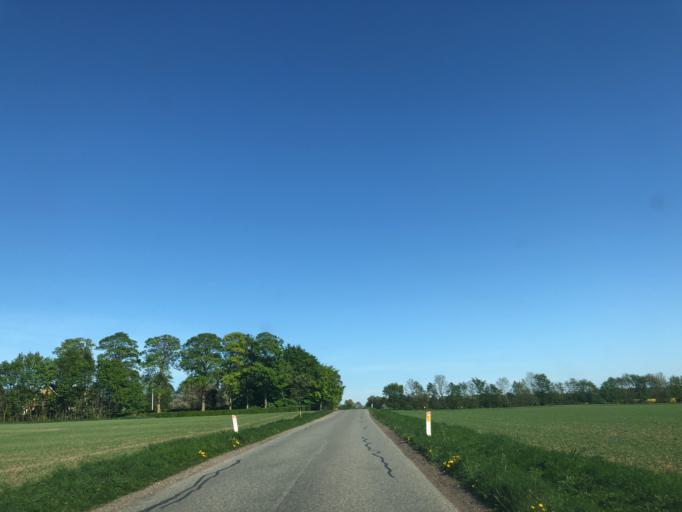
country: DK
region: Zealand
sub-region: Ringsted Kommune
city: Ringsted
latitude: 55.4504
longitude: 11.7183
